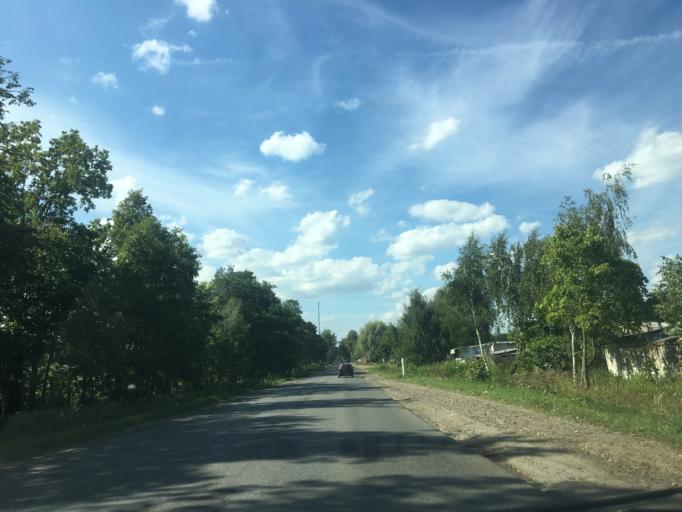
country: RU
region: Moskovskaya
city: Vidnoye
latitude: 55.5283
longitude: 37.6726
